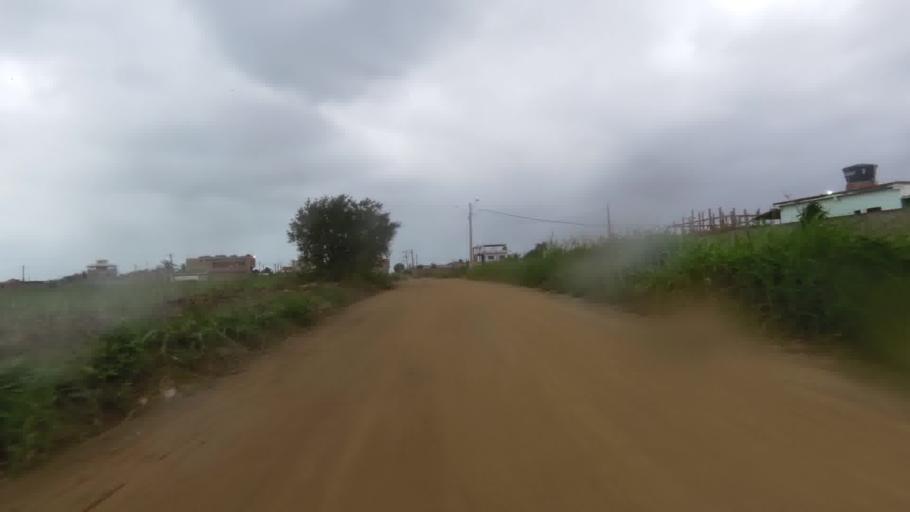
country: BR
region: Espirito Santo
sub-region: Marataizes
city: Marataizes
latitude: -21.0411
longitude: -40.8410
